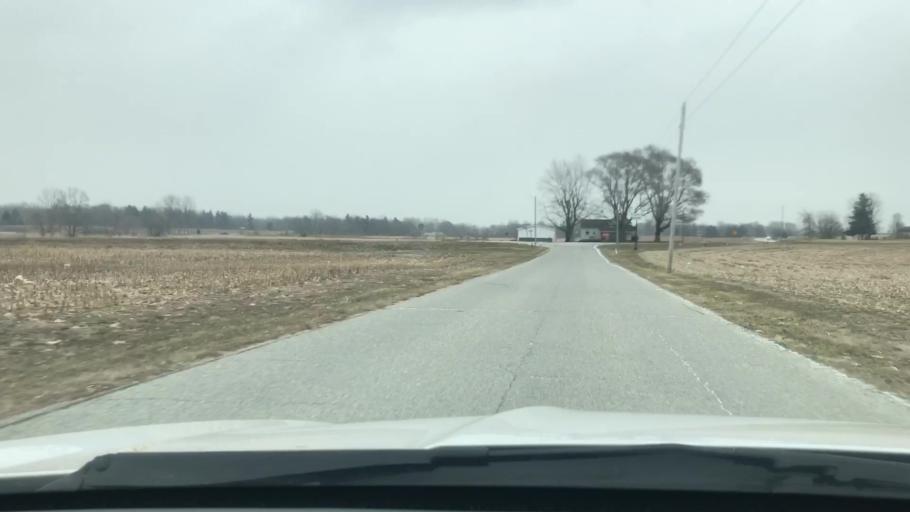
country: US
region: Indiana
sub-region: Fulton County
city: Akron
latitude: 41.0405
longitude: -86.0881
